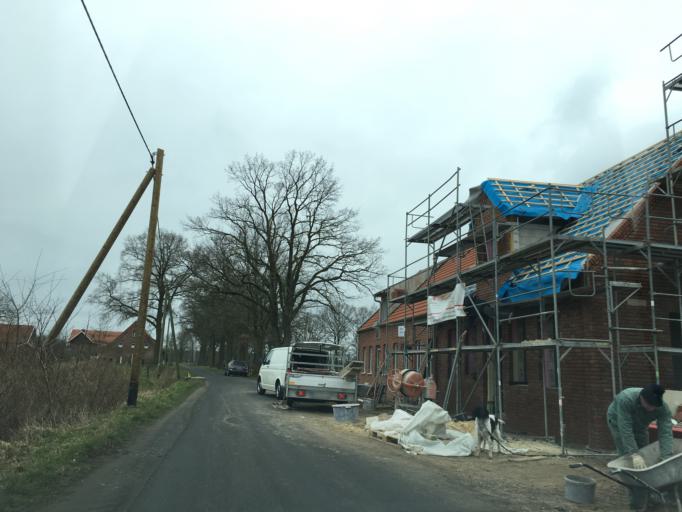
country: DE
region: North Rhine-Westphalia
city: Ludinghausen
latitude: 51.7642
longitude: 7.4726
